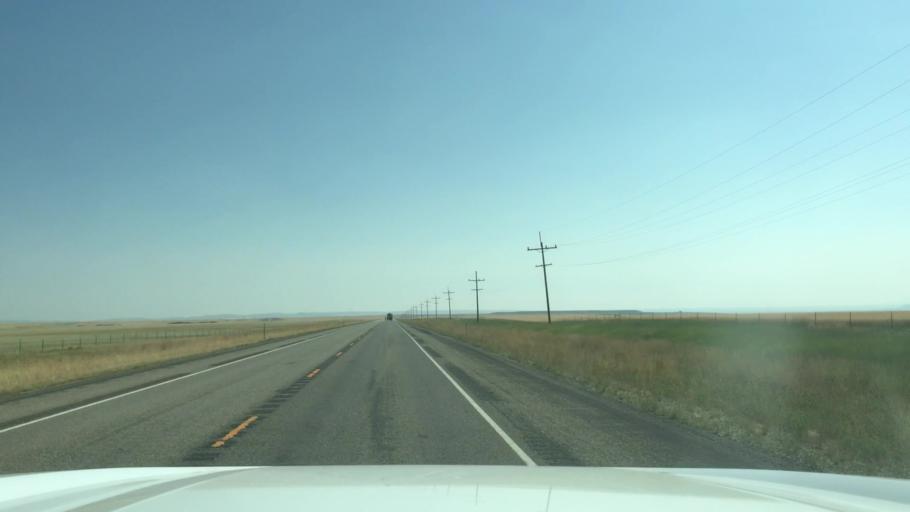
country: US
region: Montana
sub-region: Wheatland County
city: Harlowton
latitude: 46.5095
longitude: -109.7661
